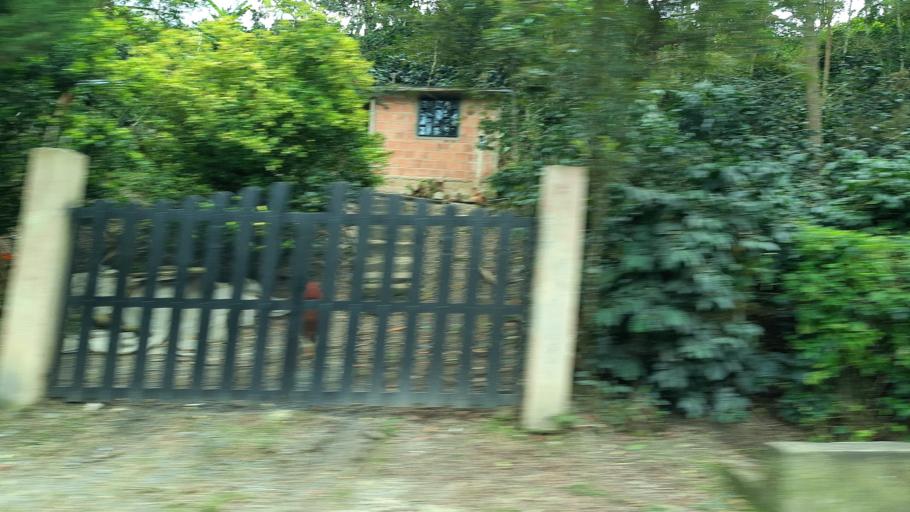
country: CO
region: Boyaca
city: Moniquira
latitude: 5.8405
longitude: -73.5873
